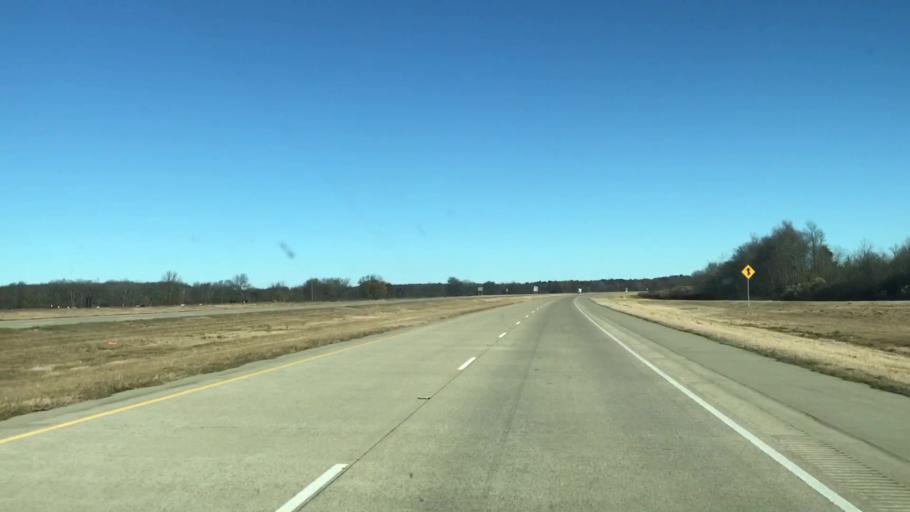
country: US
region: Louisiana
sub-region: Caddo Parish
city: Oil City
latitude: 32.7704
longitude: -93.8886
